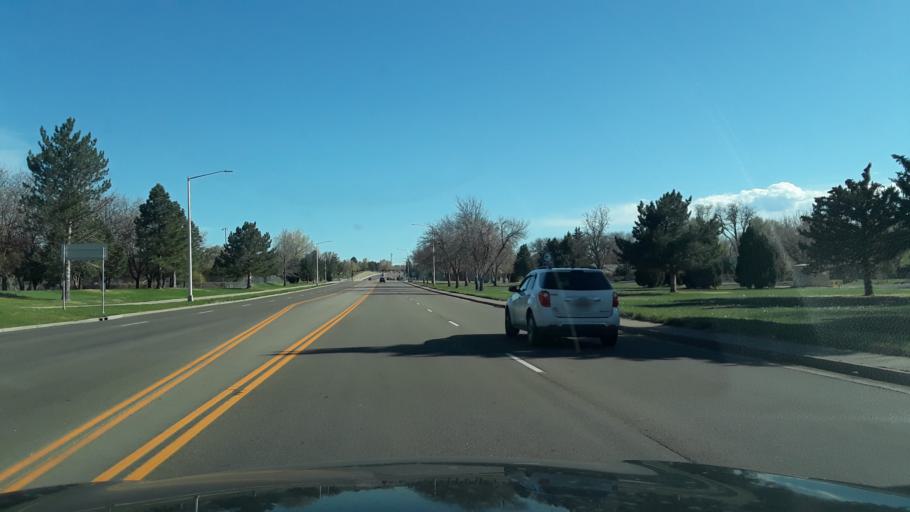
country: US
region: Colorado
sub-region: Pueblo County
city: Pueblo
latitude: 38.2627
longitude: -104.6618
